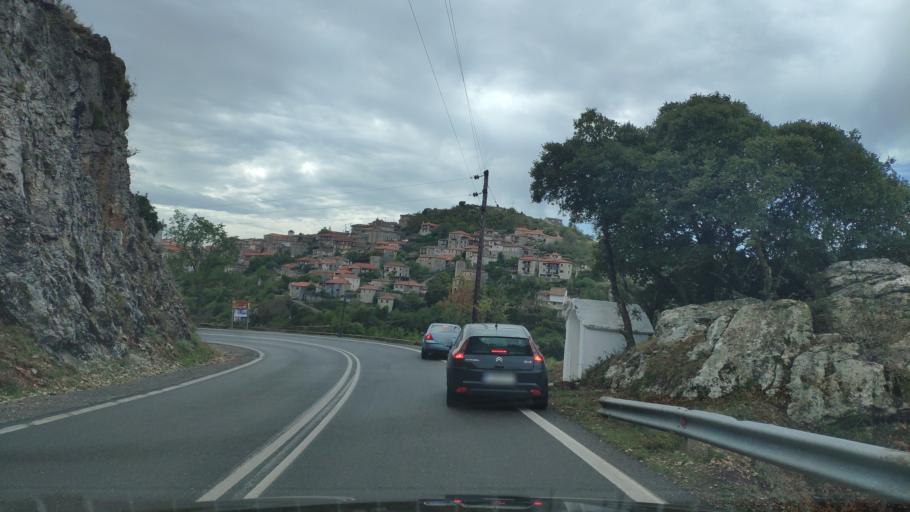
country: GR
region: Peloponnese
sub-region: Nomos Arkadias
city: Dimitsana
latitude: 37.6010
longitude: 22.0388
